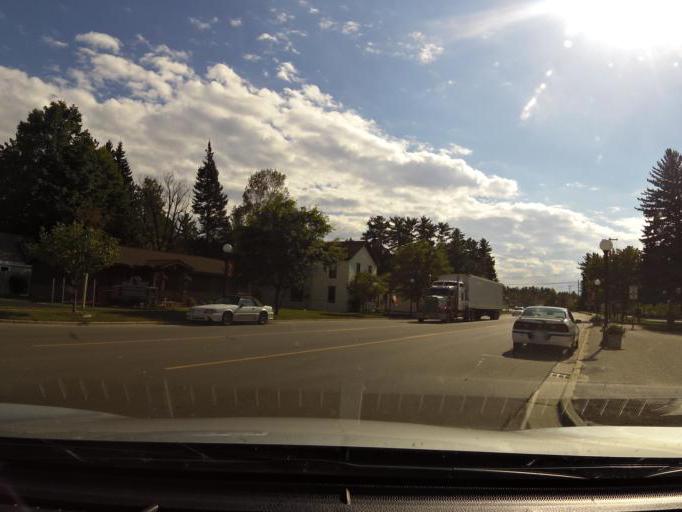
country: US
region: Michigan
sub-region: Roscommon County
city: Roscommon
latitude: 44.4964
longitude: -84.5951
